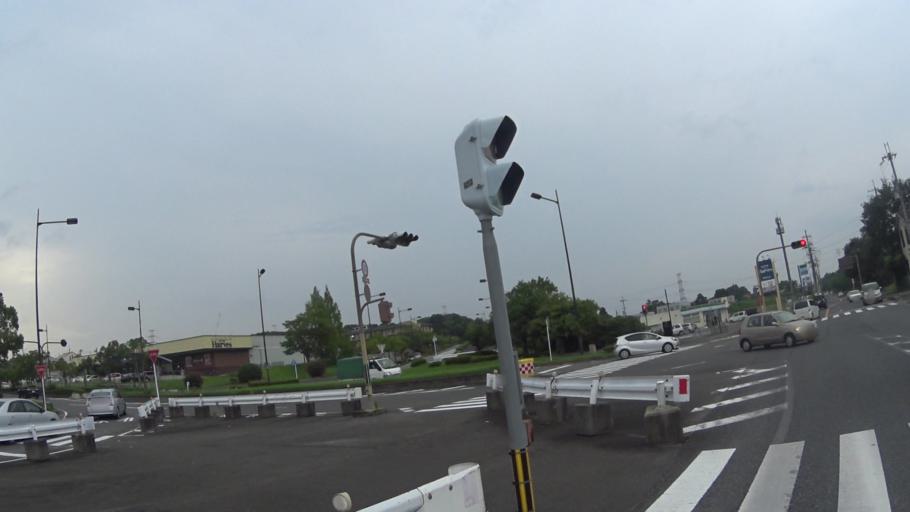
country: JP
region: Nara
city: Nara-shi
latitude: 34.7451
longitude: 135.7946
